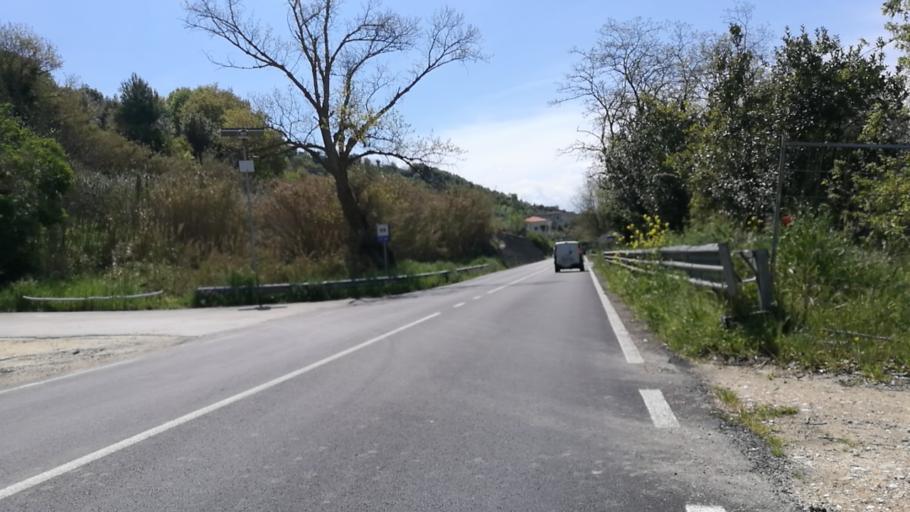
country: IT
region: Abruzzo
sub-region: Provincia di Chieti
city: San Vito Chietino
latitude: 42.2973
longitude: 14.4411
